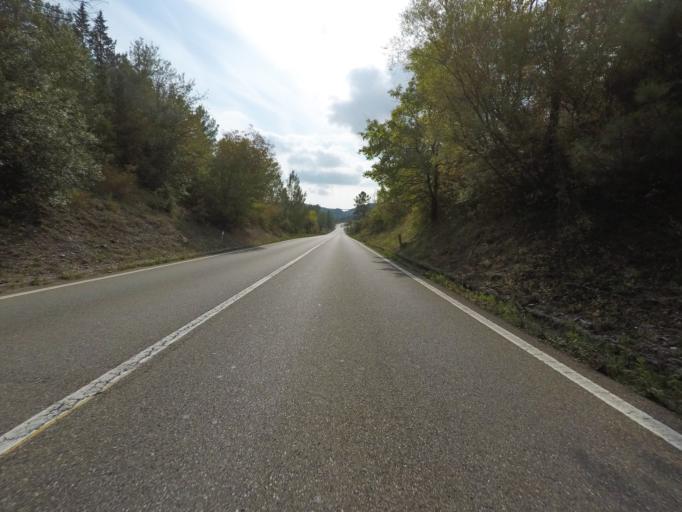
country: IT
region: Tuscany
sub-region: Provincia di Siena
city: Murlo
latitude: 43.1229
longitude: 11.2965
